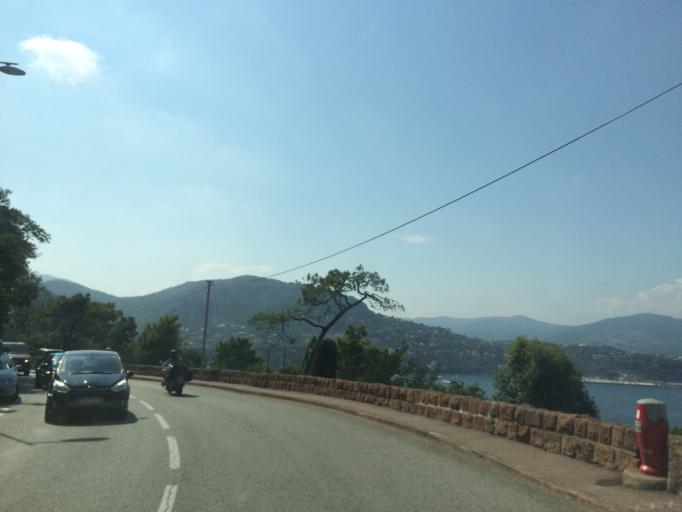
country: FR
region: Provence-Alpes-Cote d'Azur
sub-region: Departement des Alpes-Maritimes
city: Theoule-sur-Mer
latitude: 43.5050
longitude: 6.9524
